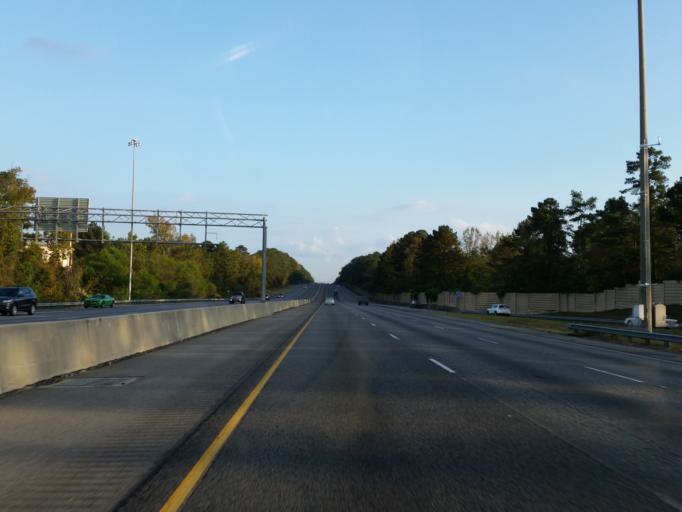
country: US
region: Georgia
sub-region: Bibb County
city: West Point
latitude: 32.8779
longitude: -83.7668
